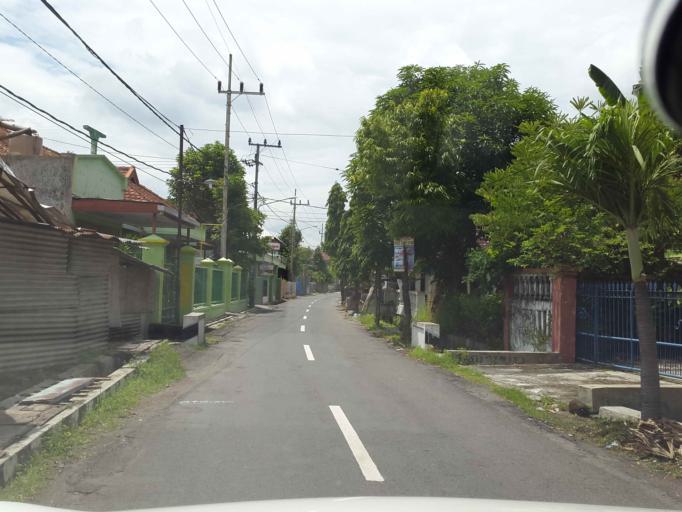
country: ID
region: East Java
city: Mojokerto
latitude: -7.4515
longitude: 112.4472
